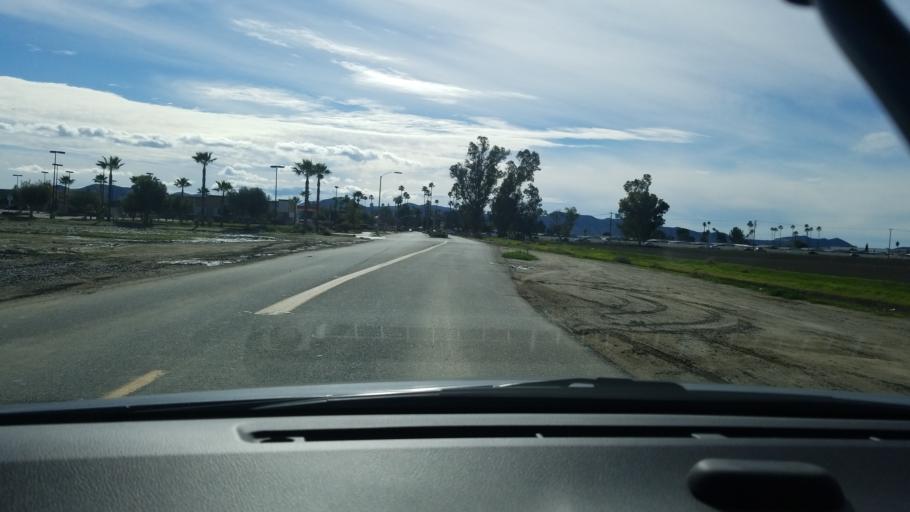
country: US
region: California
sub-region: Riverside County
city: Hemet
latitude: 33.7467
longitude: -117.0241
